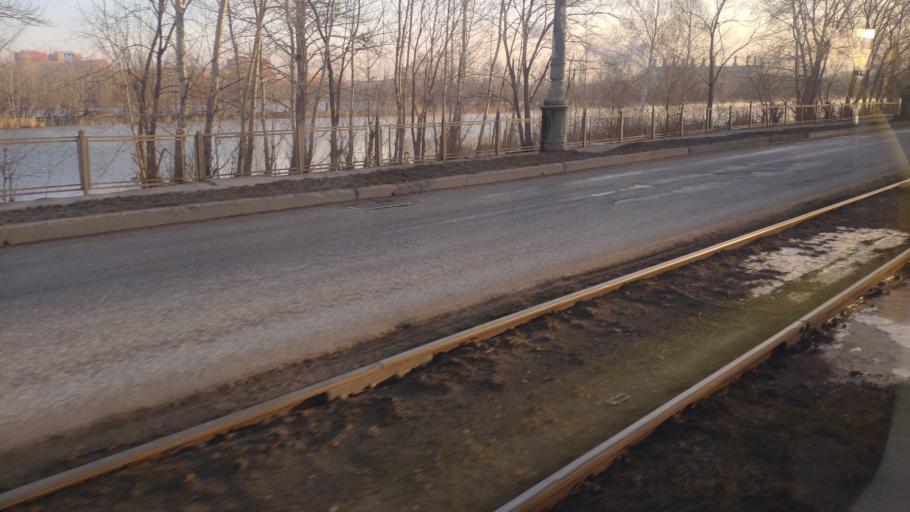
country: RU
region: Chelyabinsk
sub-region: Gorod Magnitogorsk
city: Magnitogorsk
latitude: 53.4223
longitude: 59.0171
